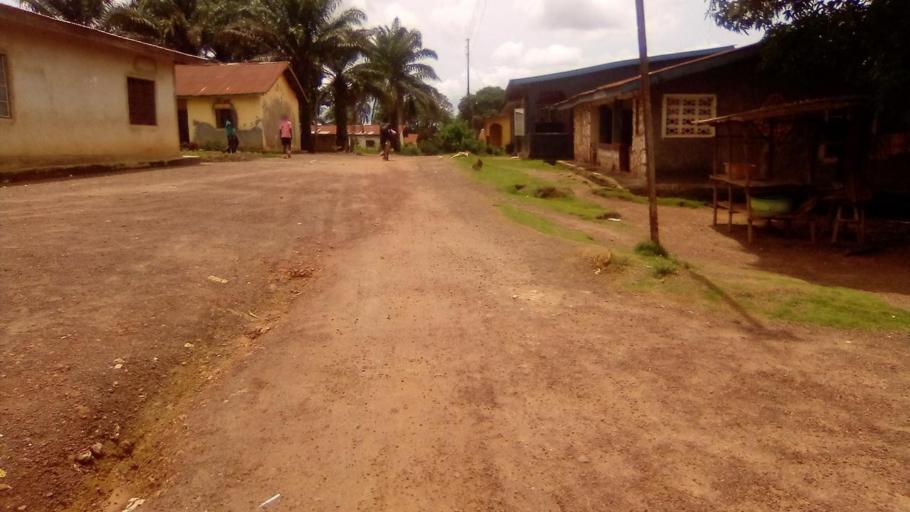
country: SL
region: Southern Province
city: Bo
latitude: 7.9363
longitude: -11.7345
